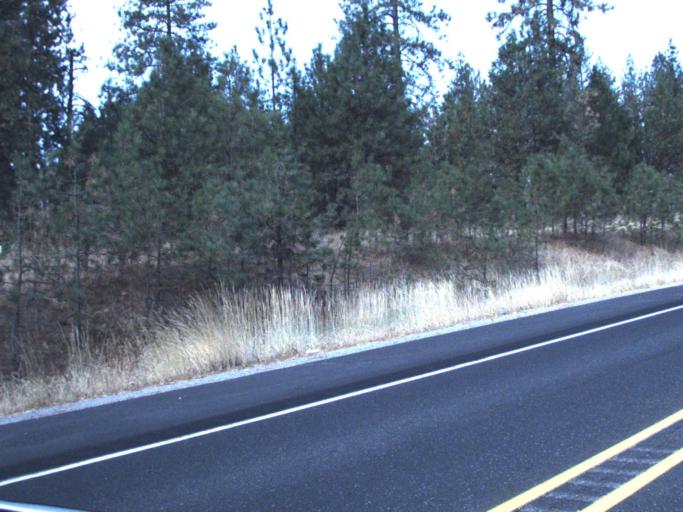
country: US
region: Washington
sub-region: Spokane County
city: Deer Park
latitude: 47.9287
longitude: -117.4639
